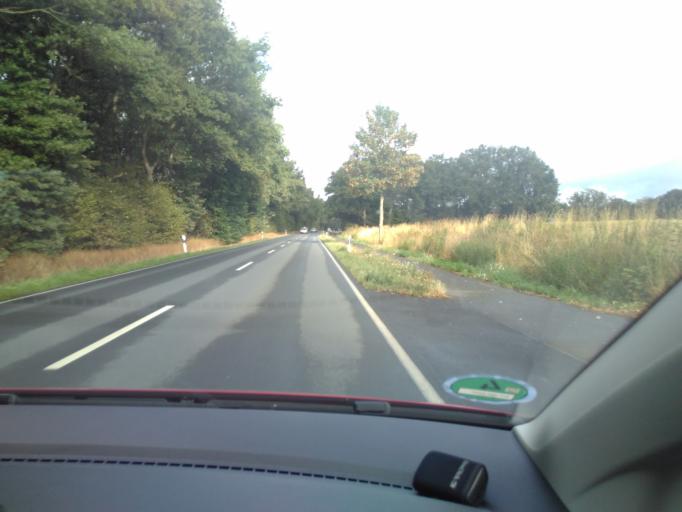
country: DE
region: North Rhine-Westphalia
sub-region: Regierungsbezirk Munster
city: Warendorf
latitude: 51.9721
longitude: 7.9617
